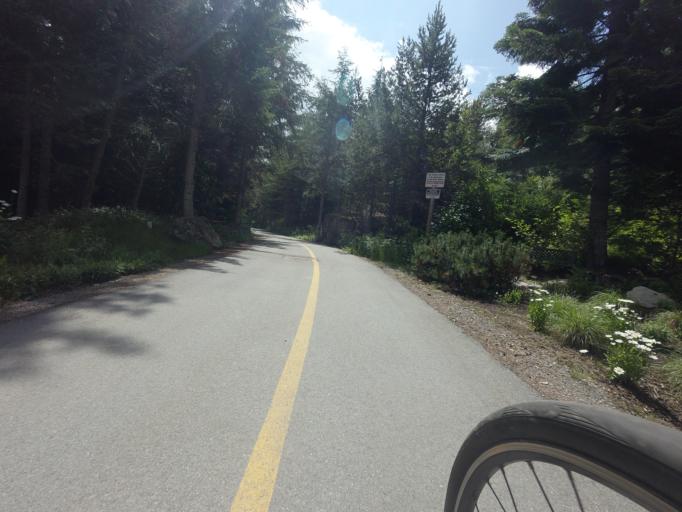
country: CA
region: British Columbia
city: Whistler
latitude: 50.1137
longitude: -122.9682
